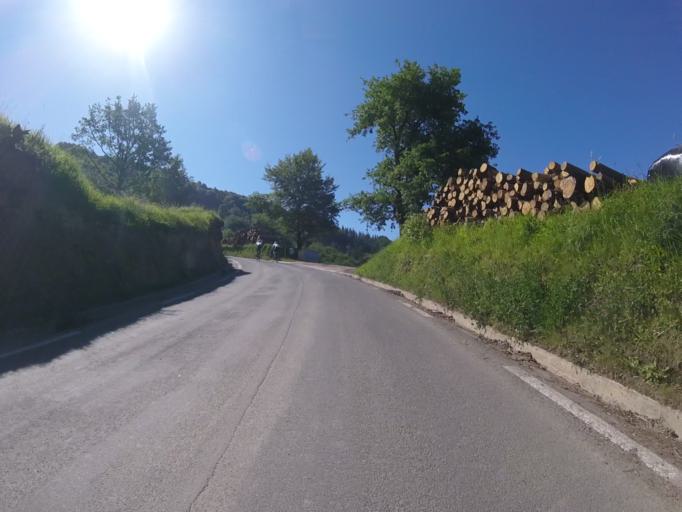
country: ES
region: Basque Country
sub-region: Provincia de Guipuzcoa
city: Beizama
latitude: 43.1295
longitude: -2.1975
